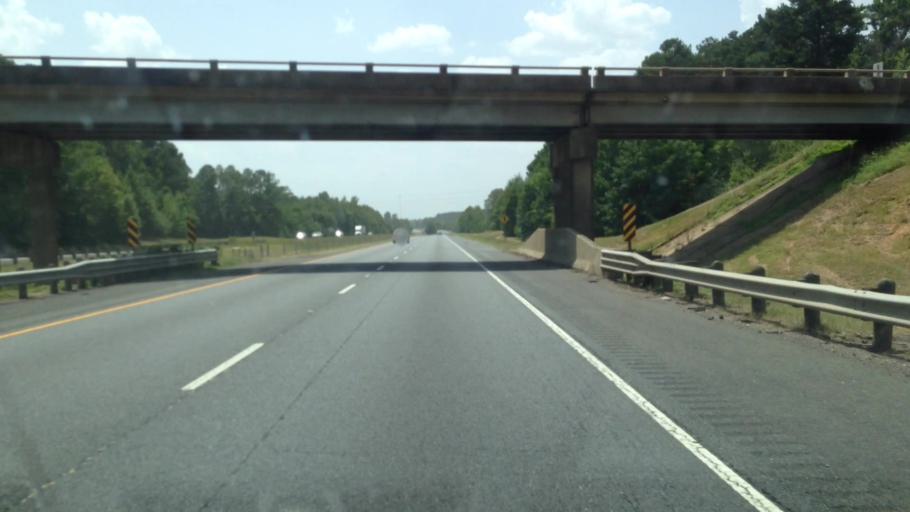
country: US
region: Louisiana
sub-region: Lincoln Parish
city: Grambling
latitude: 32.5469
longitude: -92.7662
